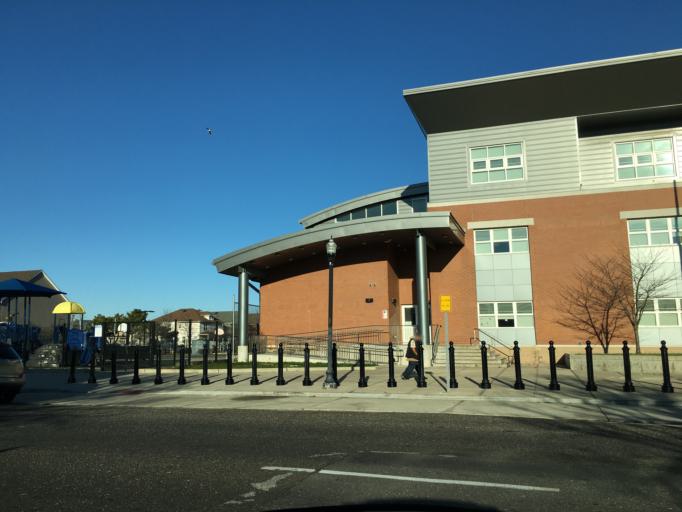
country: US
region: New Jersey
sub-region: Atlantic County
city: Atlantic City
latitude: 39.3667
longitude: -74.4256
